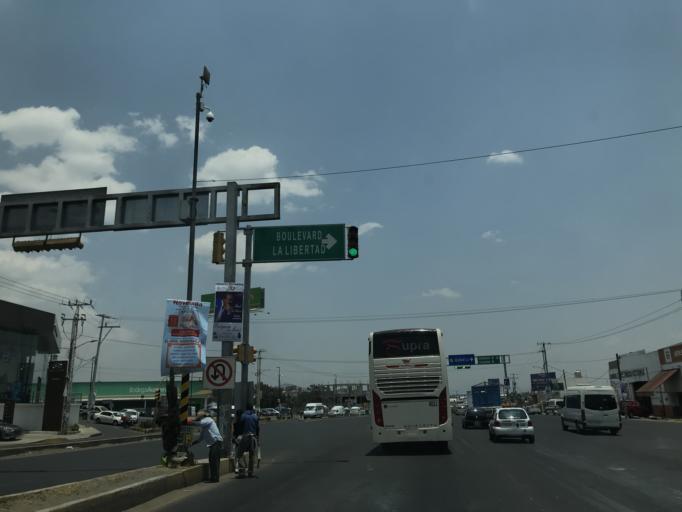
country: MX
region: Tlaxcala
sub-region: Yauhquemehcan
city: Hualcaltzinco
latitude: 19.4148
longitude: -98.1606
